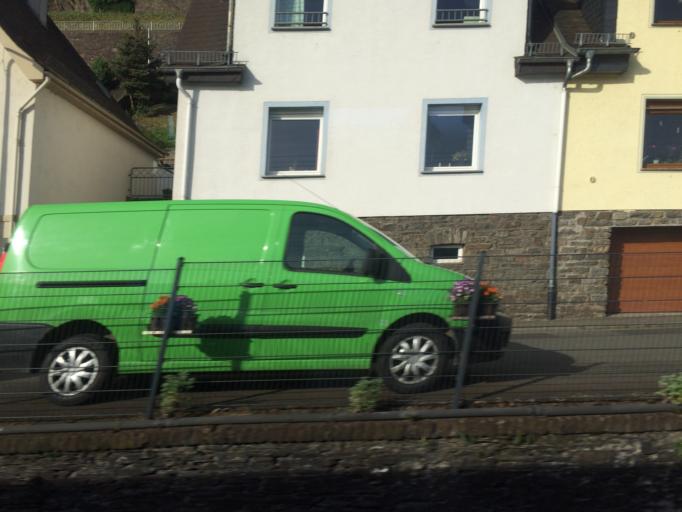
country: DE
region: Rheinland-Pfalz
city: Oberdiebach
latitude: 50.0511
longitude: 7.7865
